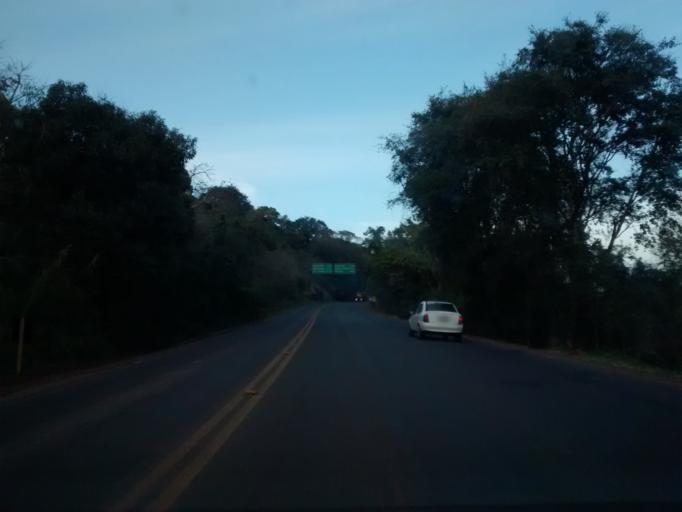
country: BR
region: Parana
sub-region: Francisco Beltrao
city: Francisco Beltrao
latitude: -26.1227
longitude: -53.0394
